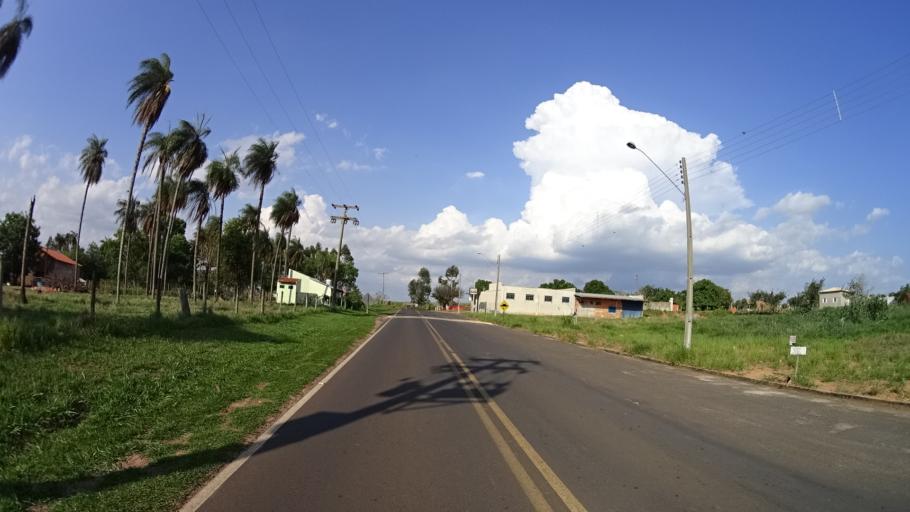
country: BR
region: Sao Paulo
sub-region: Urupes
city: Urupes
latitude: -21.3712
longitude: -49.4721
